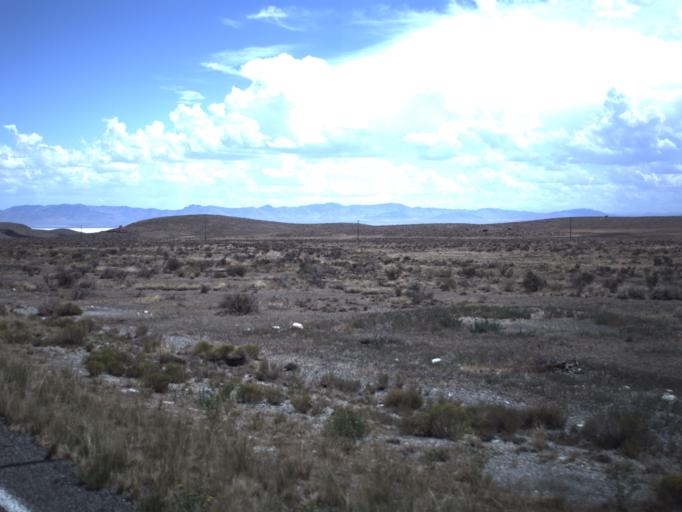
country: US
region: Utah
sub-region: Beaver County
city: Milford
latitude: 39.0370
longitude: -113.3286
